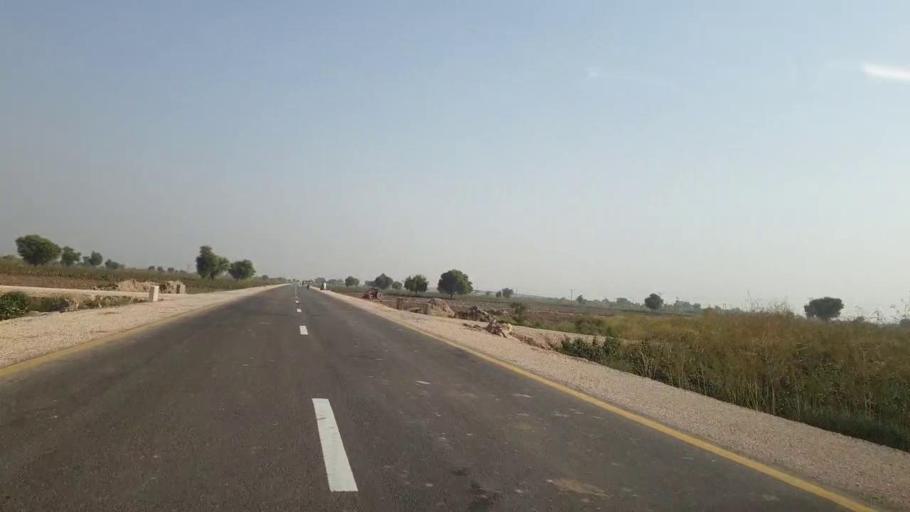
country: PK
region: Sindh
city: Sehwan
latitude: 26.4667
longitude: 67.7964
